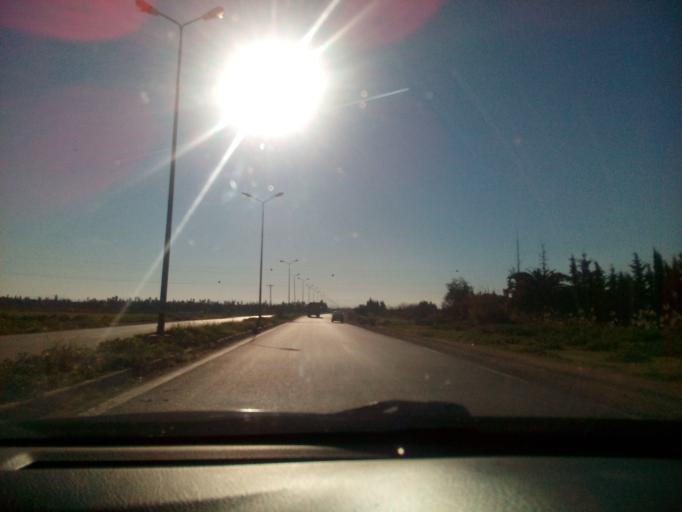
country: DZ
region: Relizane
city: Relizane
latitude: 35.7400
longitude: 0.6053
